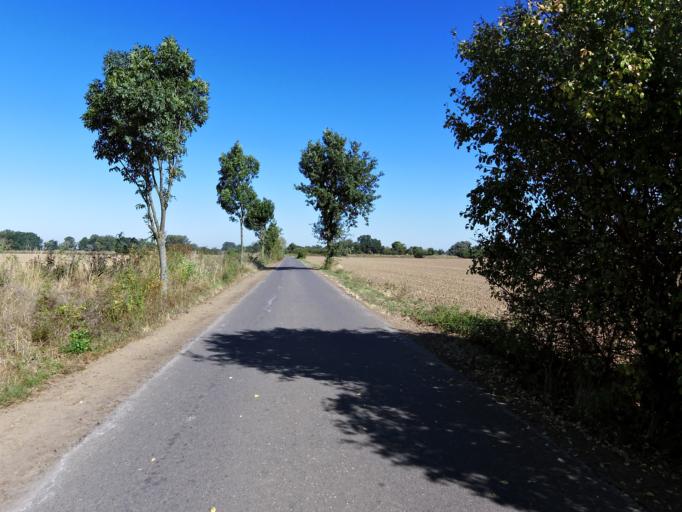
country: DE
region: Saxony
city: Elsnig
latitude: 51.6263
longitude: 12.9273
